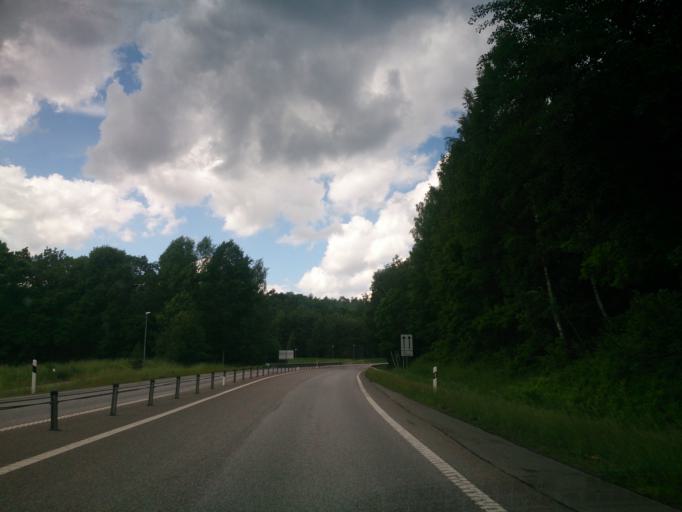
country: SE
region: OEstergoetland
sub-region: Norrkopings Kommun
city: Jursla
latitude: 58.6744
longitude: 16.1532
